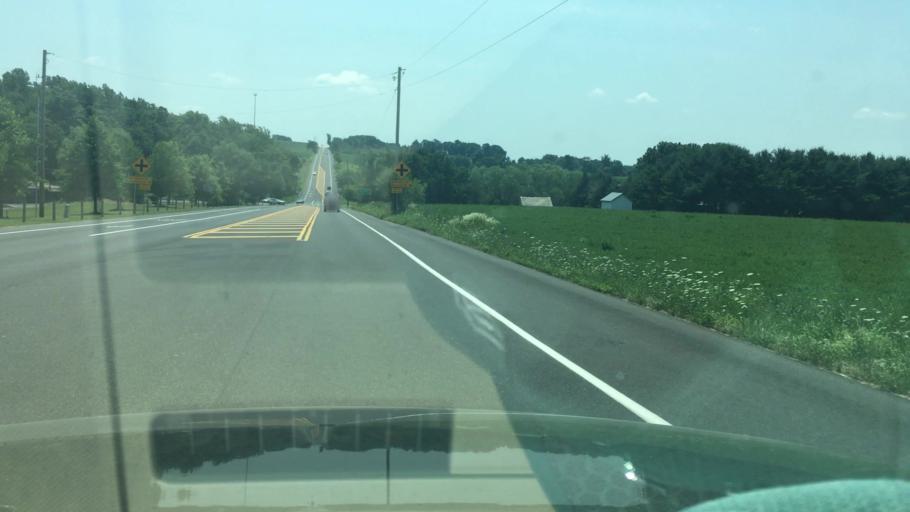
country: US
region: Pennsylvania
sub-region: Carbon County
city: Lehighton
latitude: 40.7098
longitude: -75.7632
